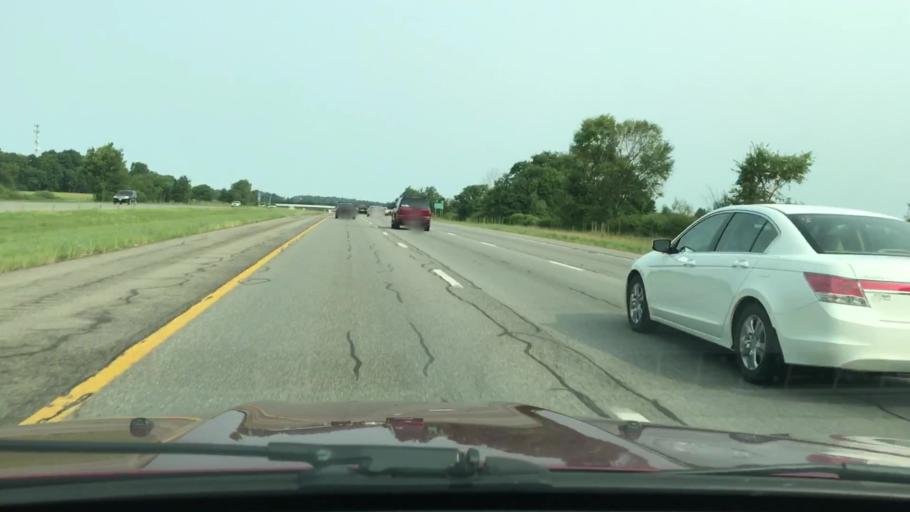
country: US
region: Ohio
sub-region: Summit County
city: Greensburg
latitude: 40.9392
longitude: -81.4415
